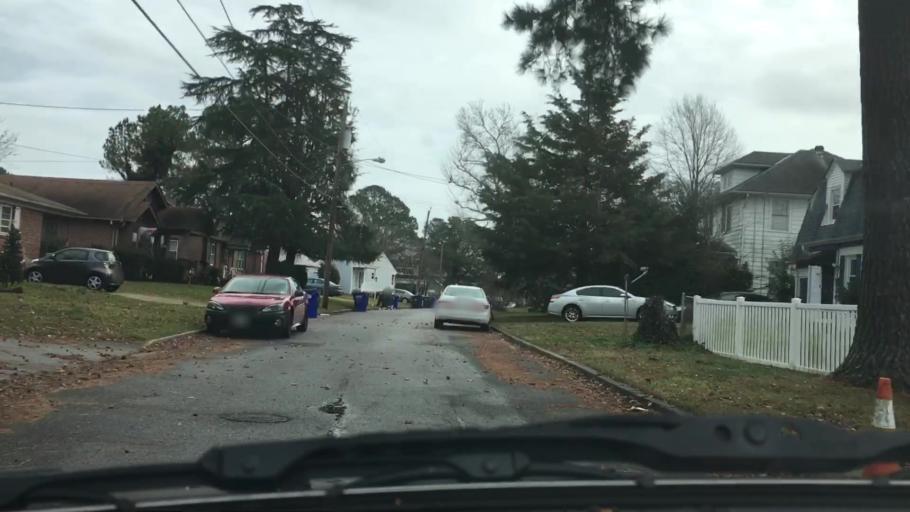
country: US
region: Virginia
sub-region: City of Norfolk
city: Norfolk
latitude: 36.8807
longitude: -76.2494
